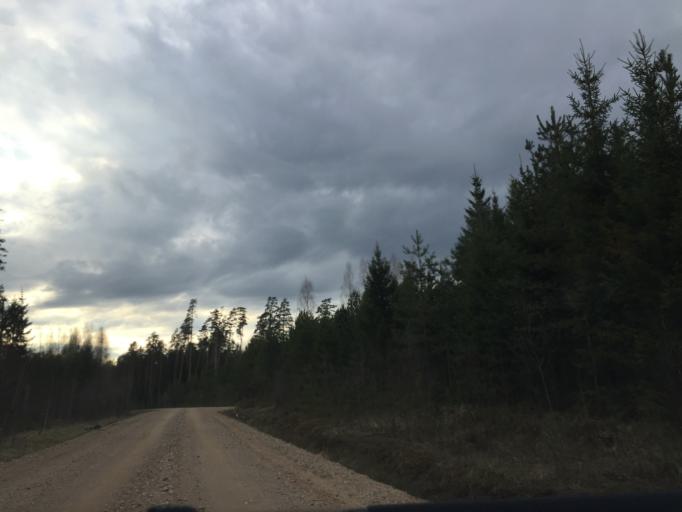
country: LV
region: Aluksnes Rajons
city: Aluksne
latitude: 57.3048
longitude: 27.0145
